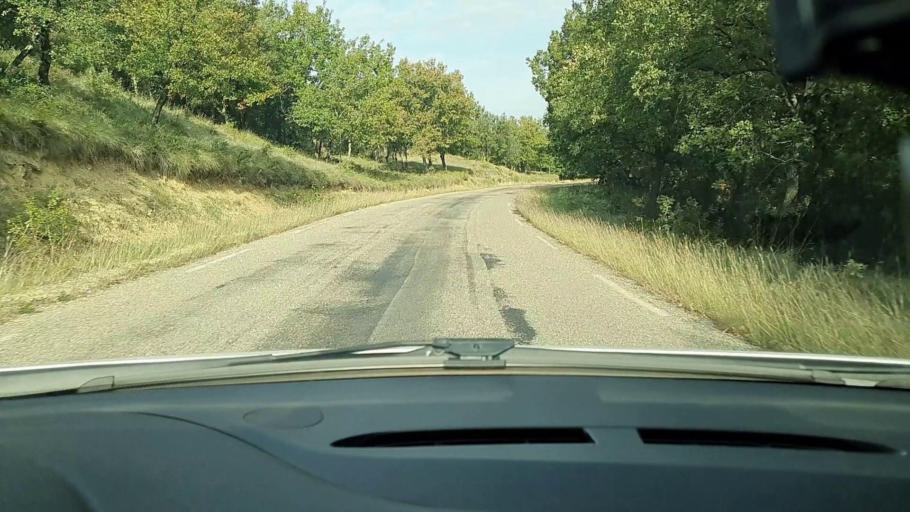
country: FR
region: Languedoc-Roussillon
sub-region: Departement du Gard
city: Saint-Quentin-la-Poterie
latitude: 44.1281
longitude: 4.4039
